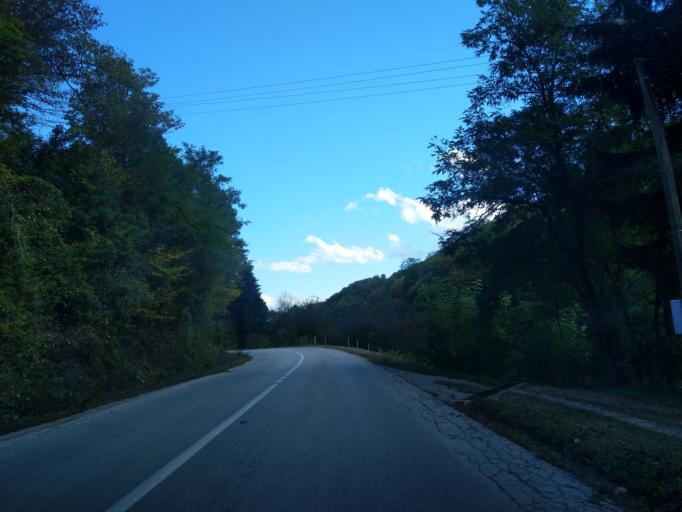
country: RS
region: Central Serbia
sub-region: Zlatiborski Okrug
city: Uzice
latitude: 43.8797
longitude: 19.7831
